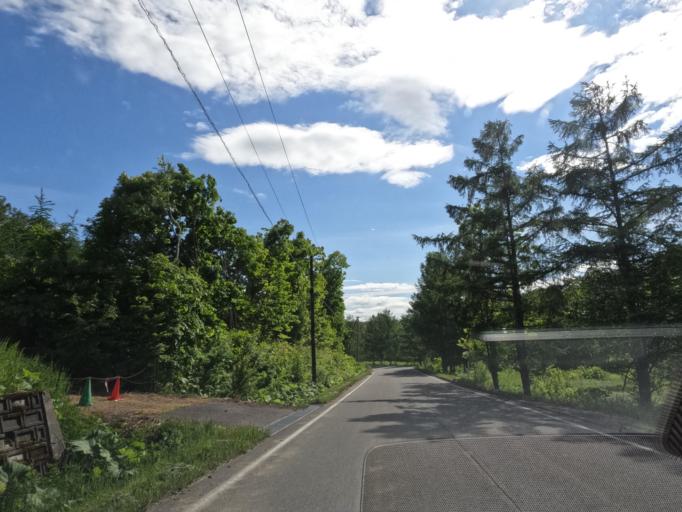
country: JP
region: Hokkaido
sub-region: Asahikawa-shi
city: Asahikawa
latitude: 43.7588
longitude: 142.5252
